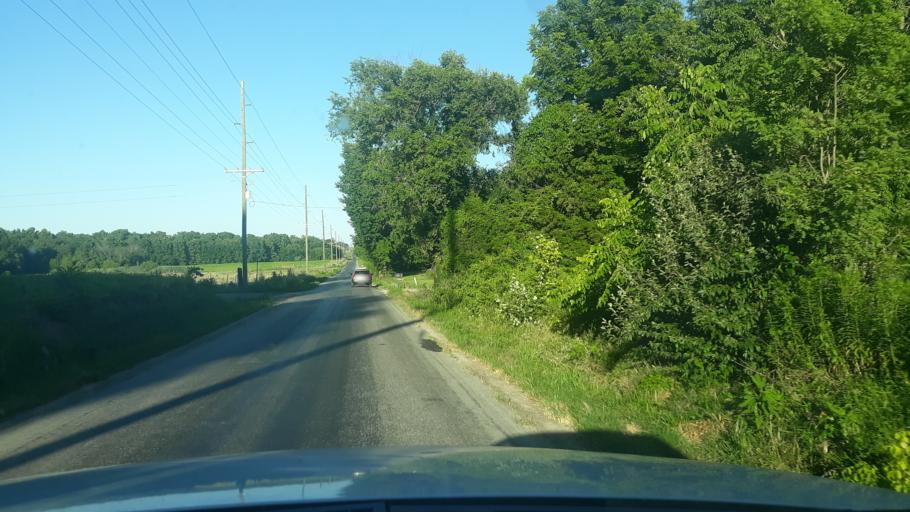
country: US
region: Illinois
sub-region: Saline County
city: Harrisburg
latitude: 37.8632
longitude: -88.5877
